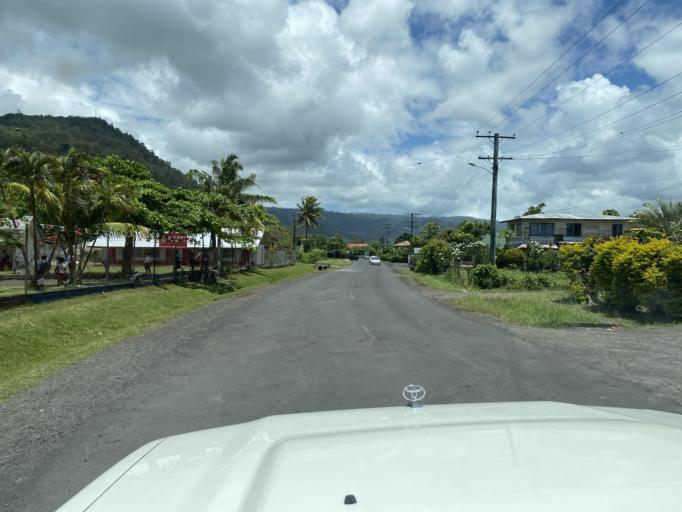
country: WS
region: Tuamasaga
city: Apia
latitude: -13.8410
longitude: -171.7741
